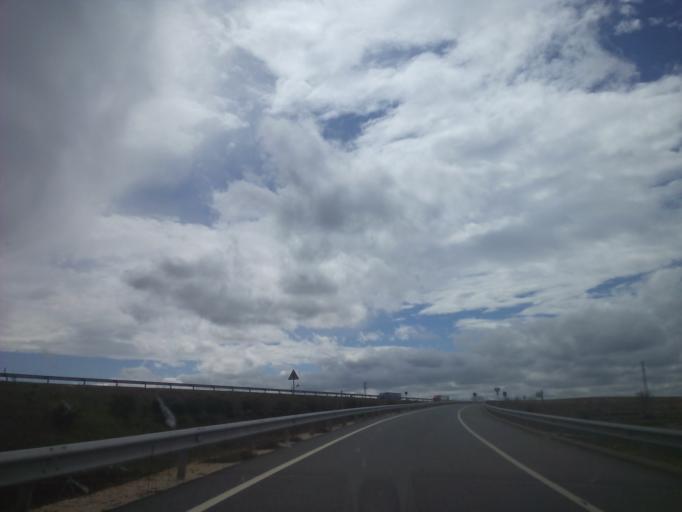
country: ES
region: Castille and Leon
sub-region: Provincia de Salamanca
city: Machacon
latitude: 40.9227
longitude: -5.5067
